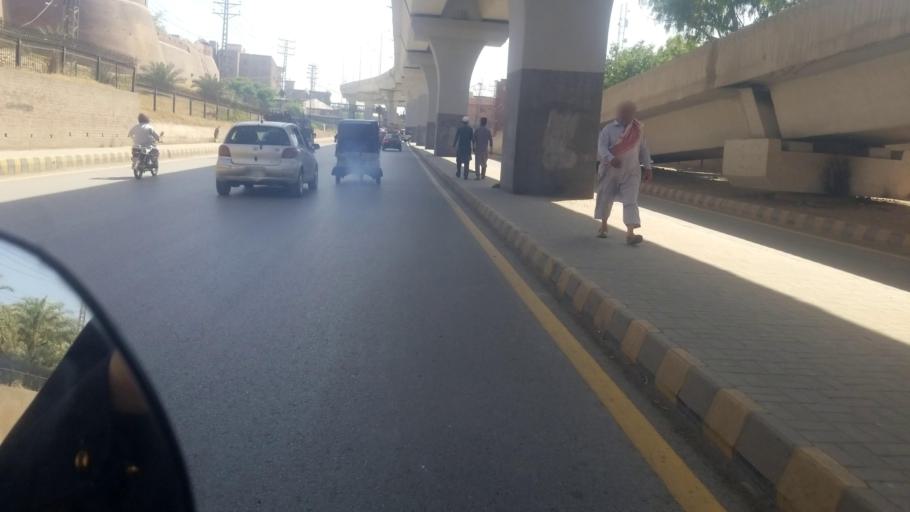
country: PK
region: Khyber Pakhtunkhwa
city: Peshawar
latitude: 34.0133
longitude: 71.5683
